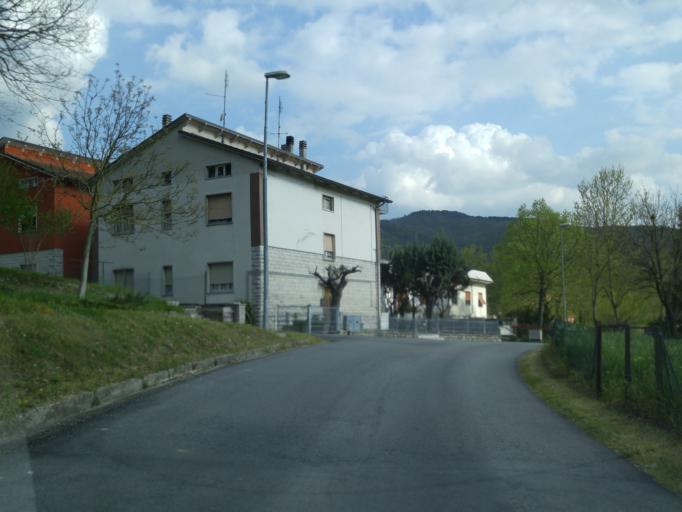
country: IT
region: The Marches
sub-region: Provincia di Pesaro e Urbino
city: Acqualagna
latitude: 43.6370
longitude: 12.6900
